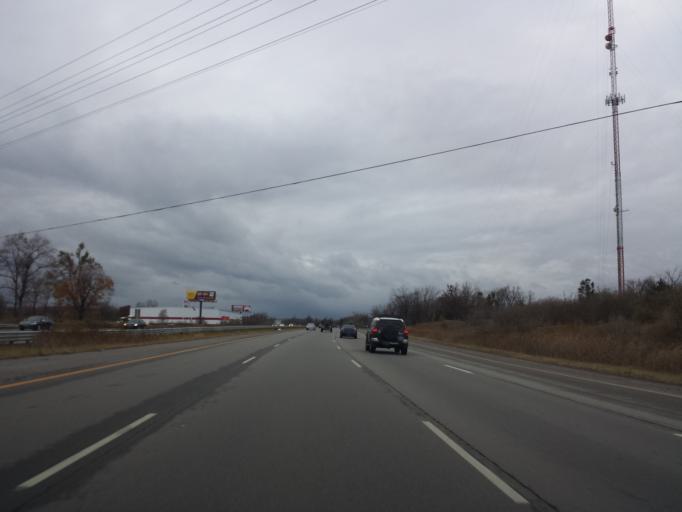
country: US
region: Michigan
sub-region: Oakland County
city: Holly
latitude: 42.7824
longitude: -83.5347
